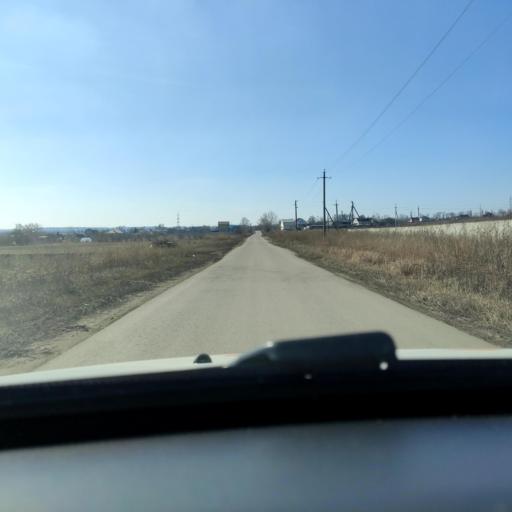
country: RU
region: Voronezj
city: Devitsa
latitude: 51.6491
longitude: 38.9543
